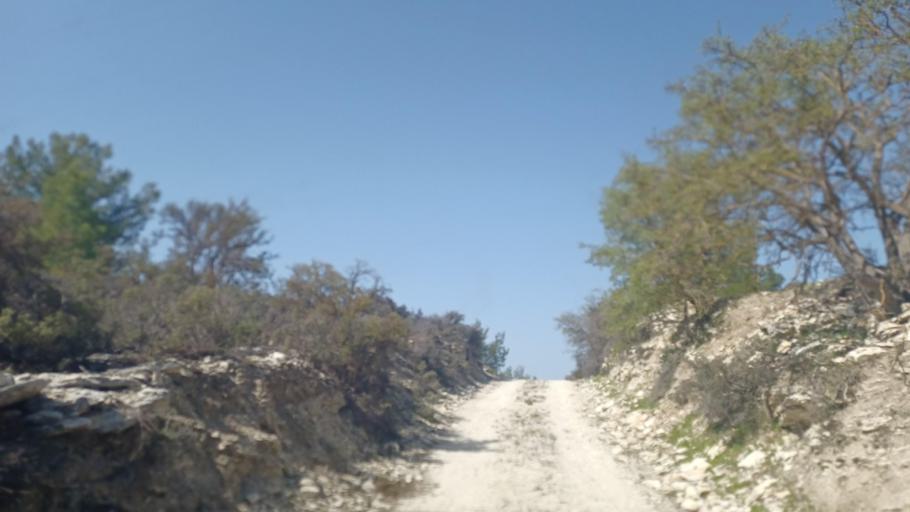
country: CY
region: Limassol
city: Pachna
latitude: 34.8827
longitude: 32.7146
